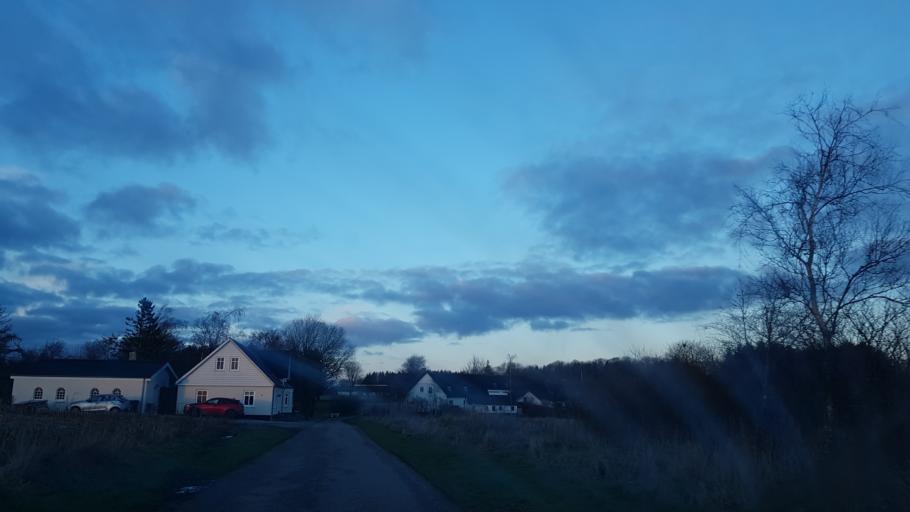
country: DK
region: South Denmark
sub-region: Kolding Kommune
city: Vamdrup
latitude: 55.3416
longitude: 9.2492
